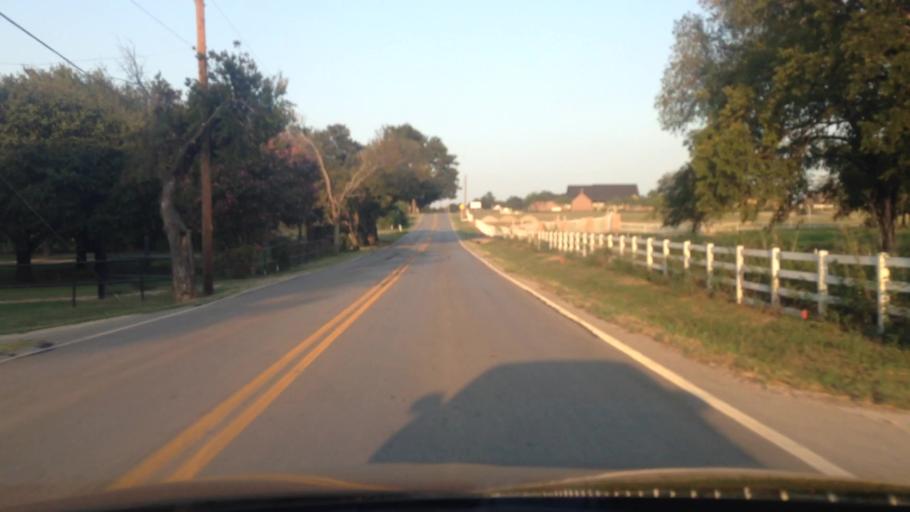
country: US
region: Texas
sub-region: Tarrant County
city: Kennedale
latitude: 32.6070
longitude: -97.2118
